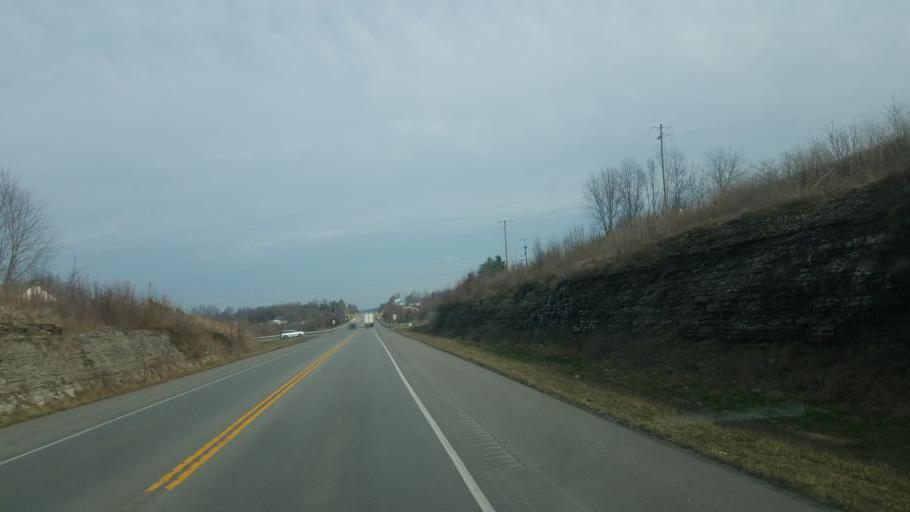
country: US
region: Kentucky
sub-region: Boyle County
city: Junction City
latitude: 37.5365
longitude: -84.8041
